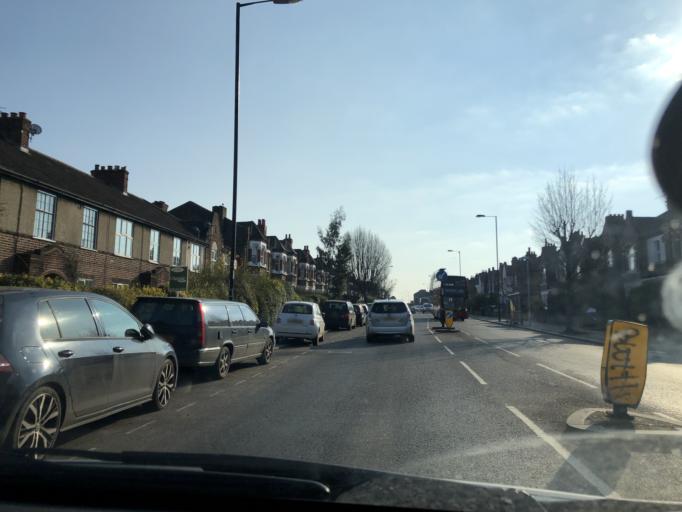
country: GB
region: England
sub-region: Greater London
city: Catford
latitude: 51.4506
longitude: -0.0401
